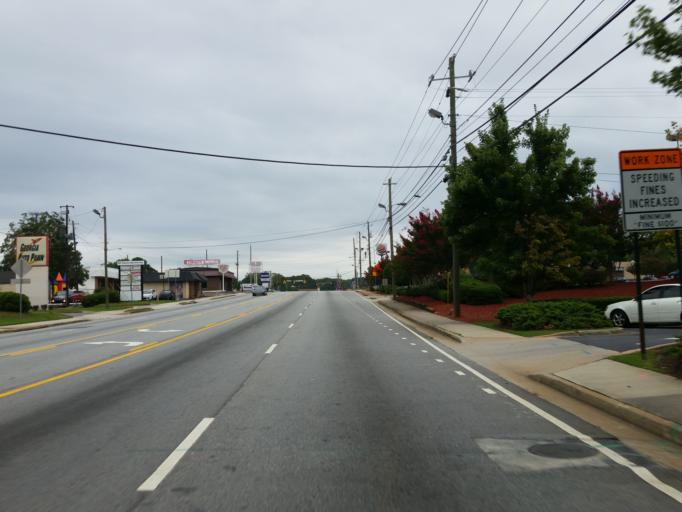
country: US
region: Georgia
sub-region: Cobb County
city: Mableton
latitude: 33.8186
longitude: -84.5791
